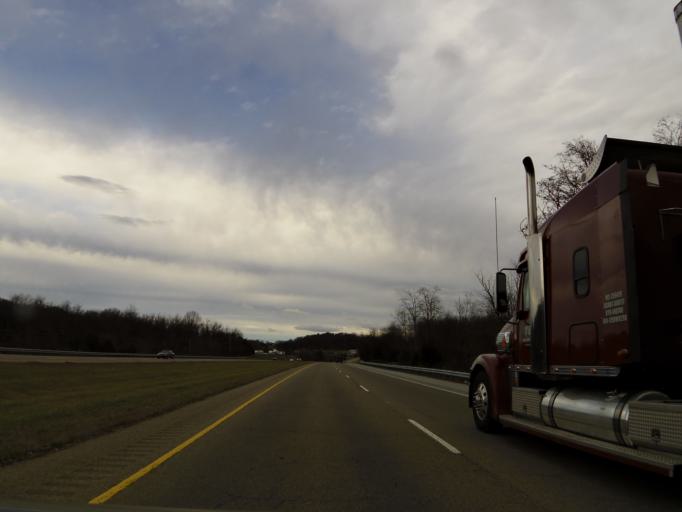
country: US
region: Tennessee
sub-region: Greene County
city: Tusculum
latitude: 36.2140
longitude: -82.7100
